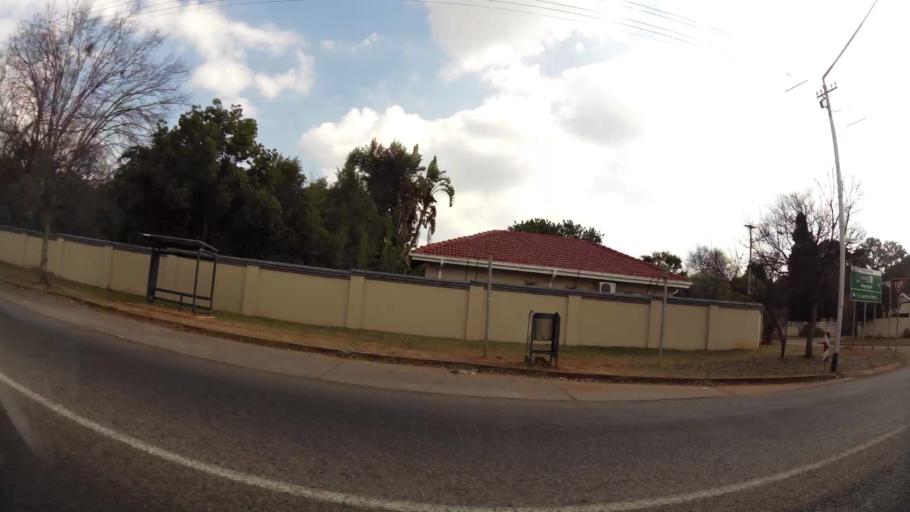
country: ZA
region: Gauteng
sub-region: City of Tshwane Metropolitan Municipality
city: Pretoria
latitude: -25.7517
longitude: 28.2885
